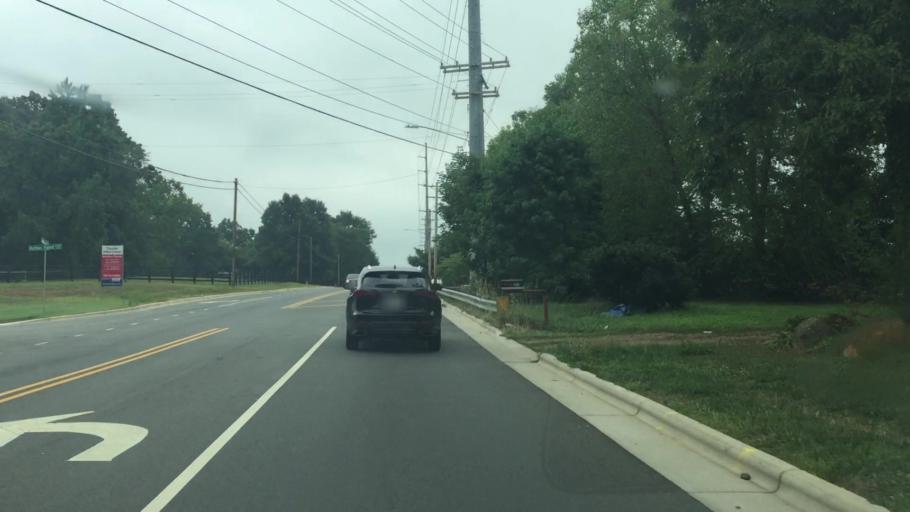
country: US
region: North Carolina
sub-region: Cabarrus County
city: Concord
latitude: 35.4144
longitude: -80.6495
